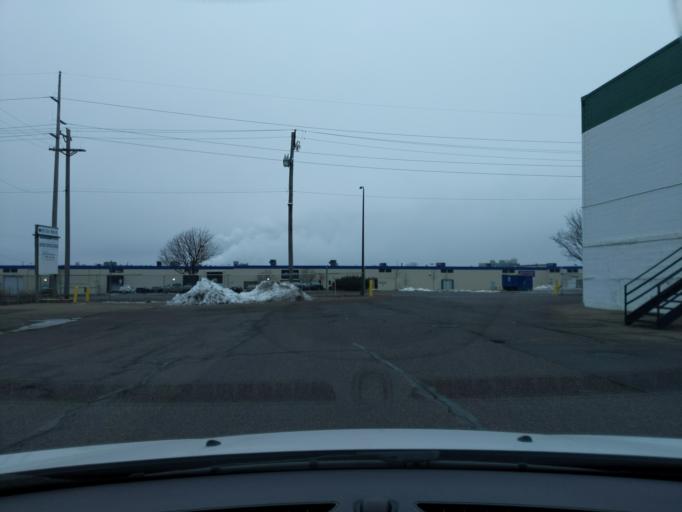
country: US
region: Minnesota
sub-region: Ramsey County
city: Falcon Heights
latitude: 44.9615
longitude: -93.1816
